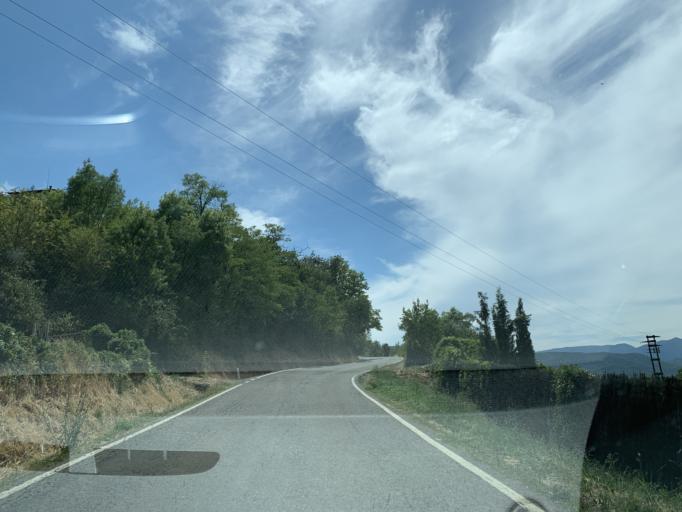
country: ES
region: Aragon
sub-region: Provincia de Huesca
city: Jaca
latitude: 42.5758
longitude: -0.5553
